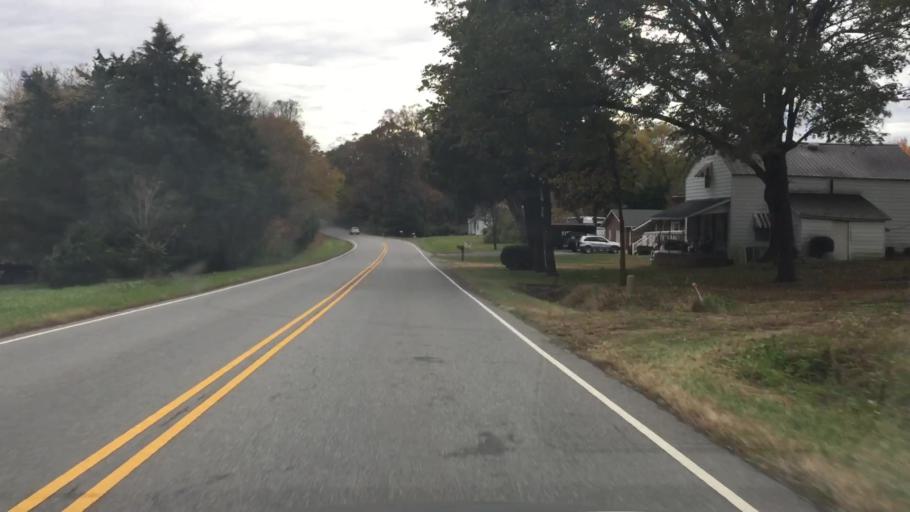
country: US
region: North Carolina
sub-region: Rockingham County
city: Reidsville
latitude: 36.2837
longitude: -79.7552
